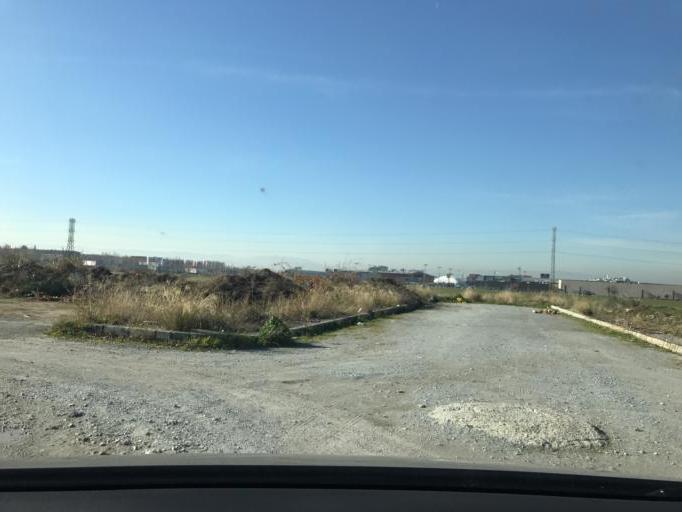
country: ES
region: Andalusia
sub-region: Provincia de Granada
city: Pulianas
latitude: 37.2158
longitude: -3.6114
